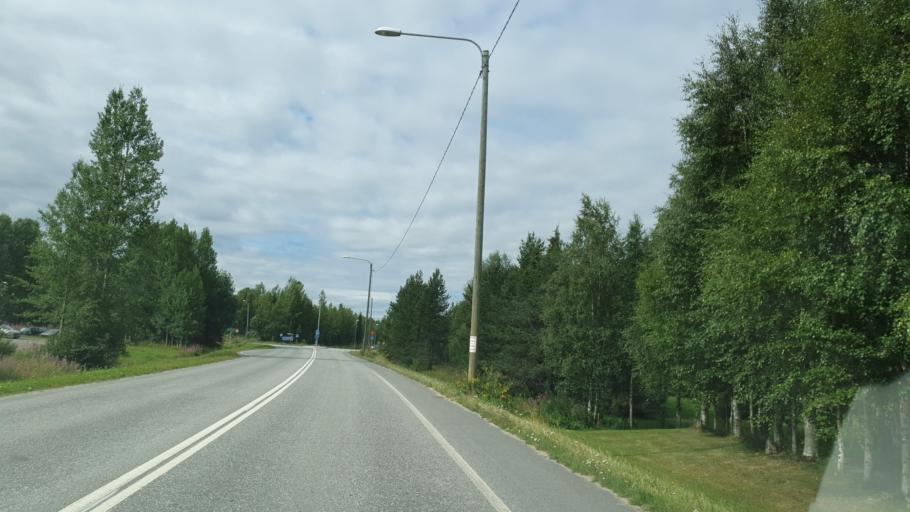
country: FI
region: Lapland
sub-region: Tunturi-Lappi
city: Kittilae
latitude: 67.6470
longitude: 24.9237
